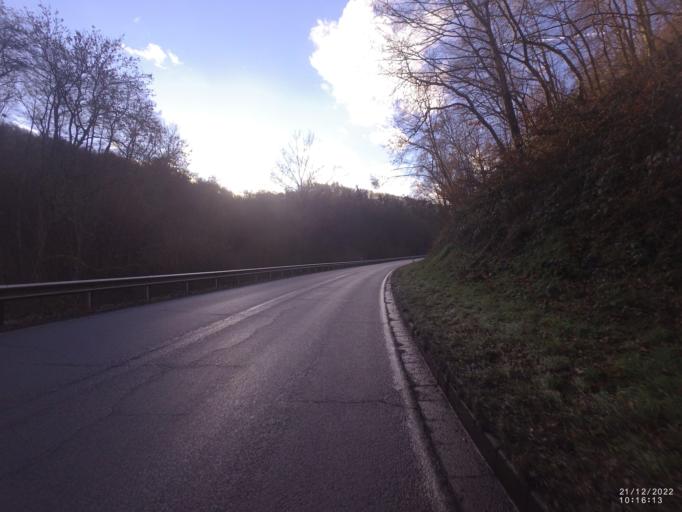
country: DE
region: Rheinland-Pfalz
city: Sinzig
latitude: 50.5240
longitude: 7.2554
